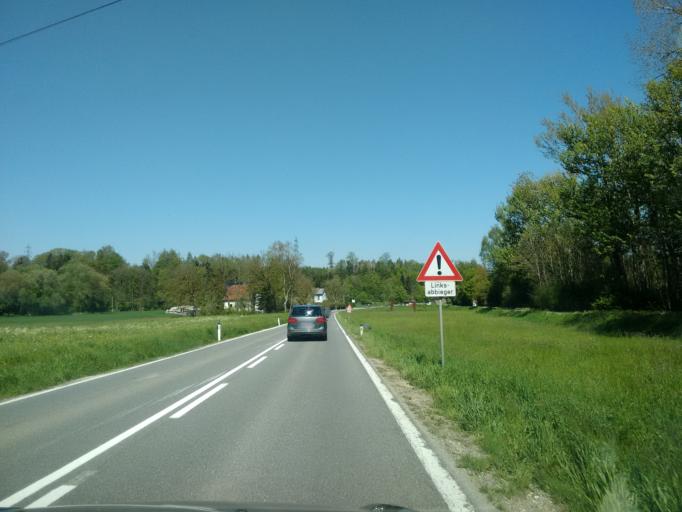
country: AT
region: Upper Austria
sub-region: Politischer Bezirk Steyr-Land
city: Bad Hall
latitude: 48.0465
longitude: 14.2067
